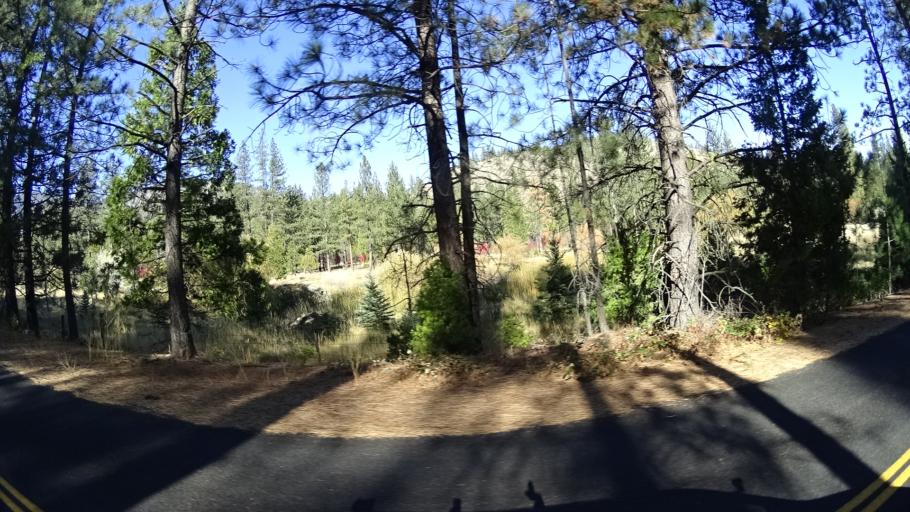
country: US
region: California
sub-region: Siskiyou County
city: Weed
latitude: 41.4338
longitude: -122.4787
